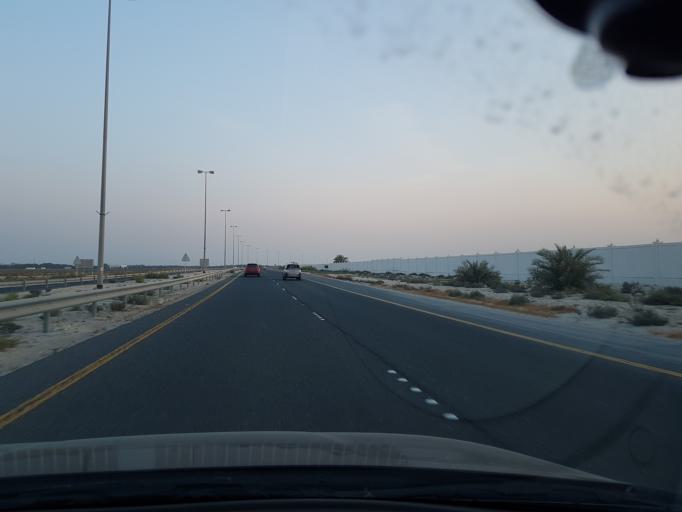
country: BH
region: Central Governorate
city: Dar Kulayb
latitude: 26.0371
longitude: 50.4998
